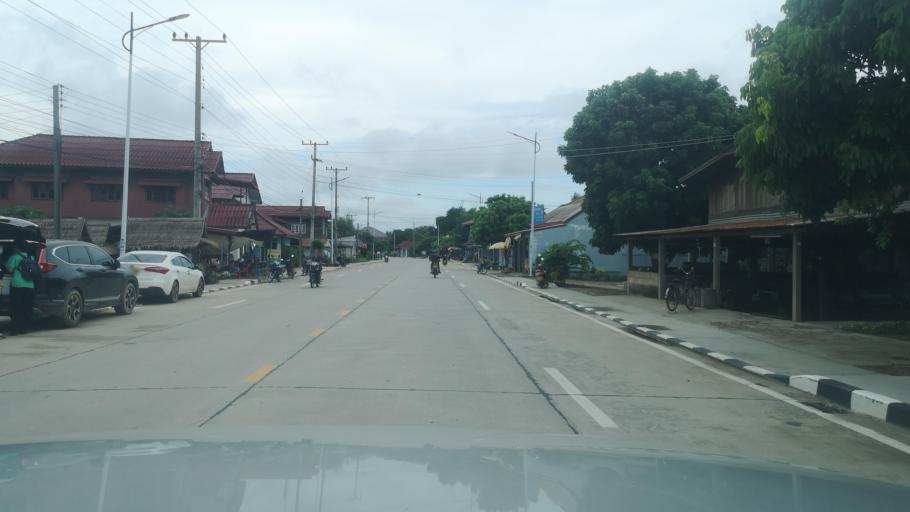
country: TH
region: Nong Khai
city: Tha Bo
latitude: 17.8275
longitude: 102.6524
